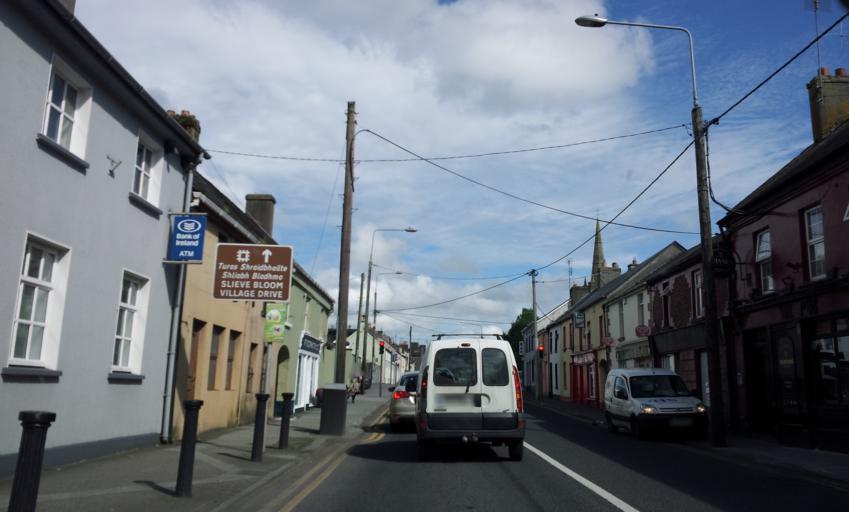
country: IE
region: Leinster
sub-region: Laois
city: Mountrath
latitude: 53.0025
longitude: -7.4752
